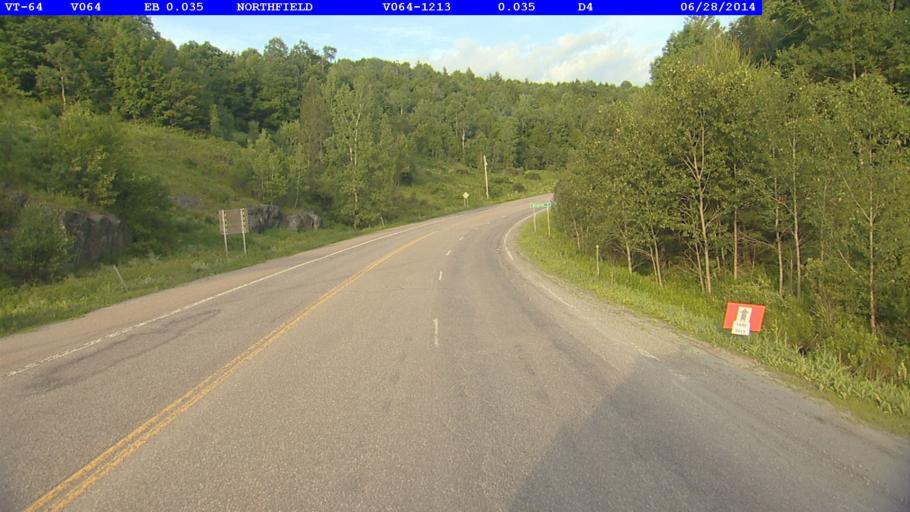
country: US
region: Vermont
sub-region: Washington County
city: Northfield
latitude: 44.1186
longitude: -72.6554
